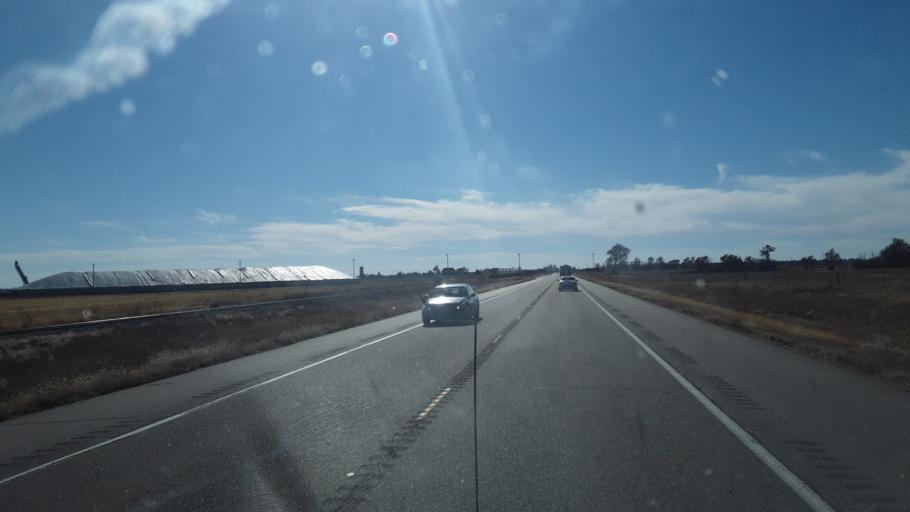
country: US
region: Kansas
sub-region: Pawnee County
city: Larned
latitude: 38.2058
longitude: -99.0630
